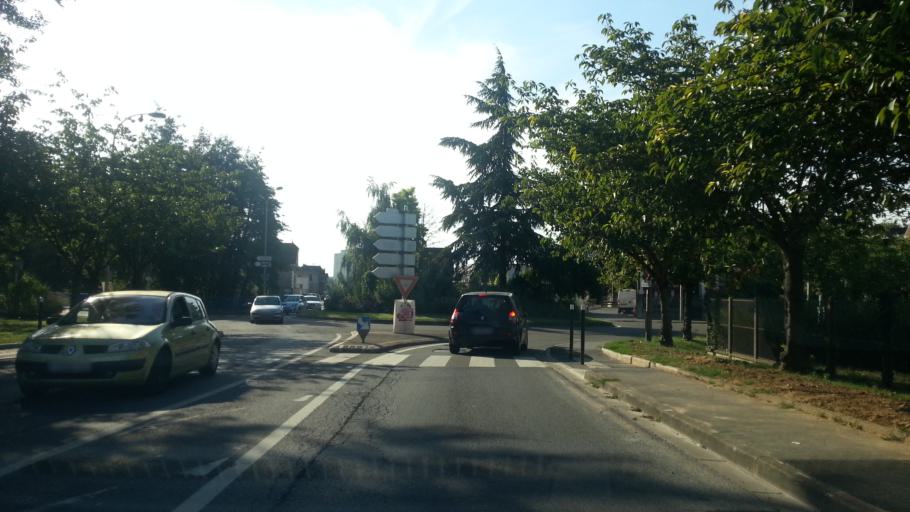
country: FR
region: Picardie
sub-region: Departement de l'Oise
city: Thiverny
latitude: 49.2550
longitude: 2.4383
